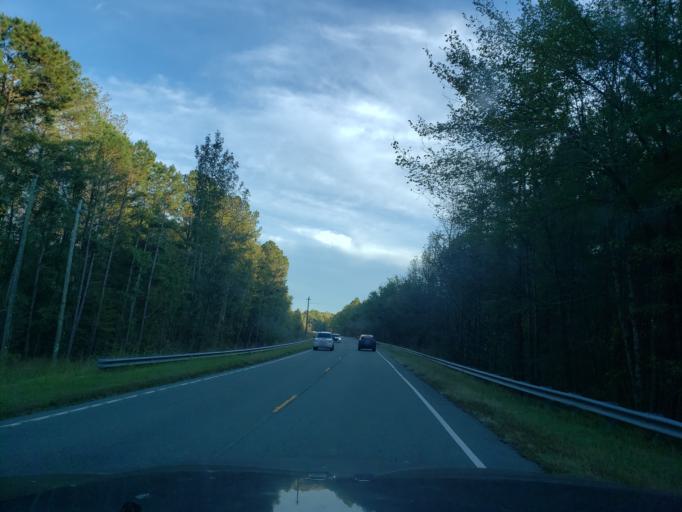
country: US
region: North Carolina
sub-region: Wake County
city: Green Level
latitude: 35.7587
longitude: -78.9630
